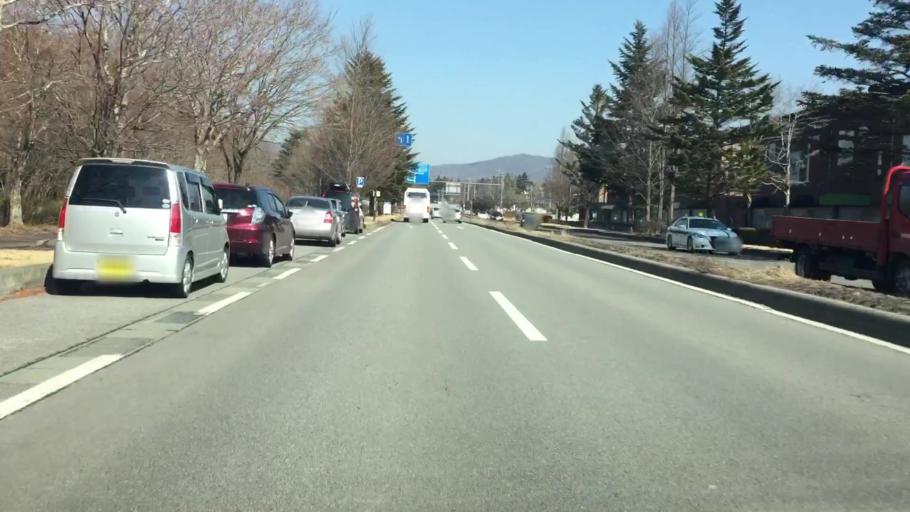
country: JP
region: Nagano
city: Saku
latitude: 36.3398
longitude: 138.6309
